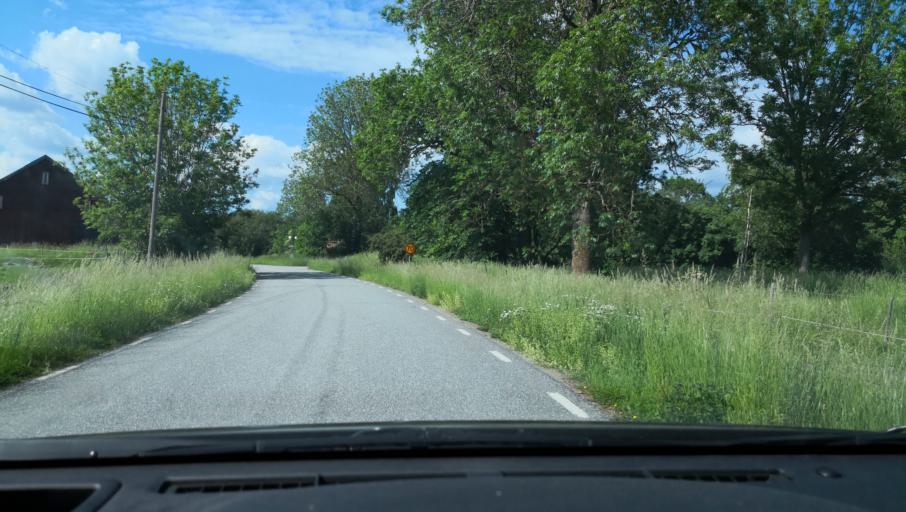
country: SE
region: Uppsala
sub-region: Enkopings Kommun
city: Orsundsbro
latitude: 59.8309
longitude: 17.3189
